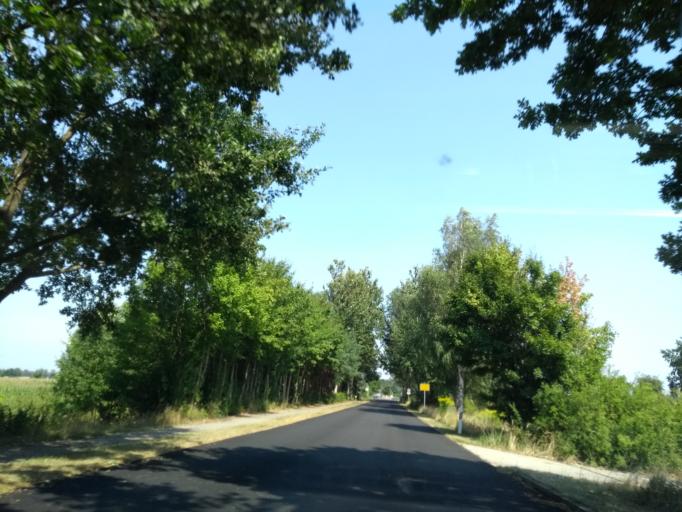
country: DE
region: Brandenburg
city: Lubbenau
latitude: 51.8429
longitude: 13.9391
